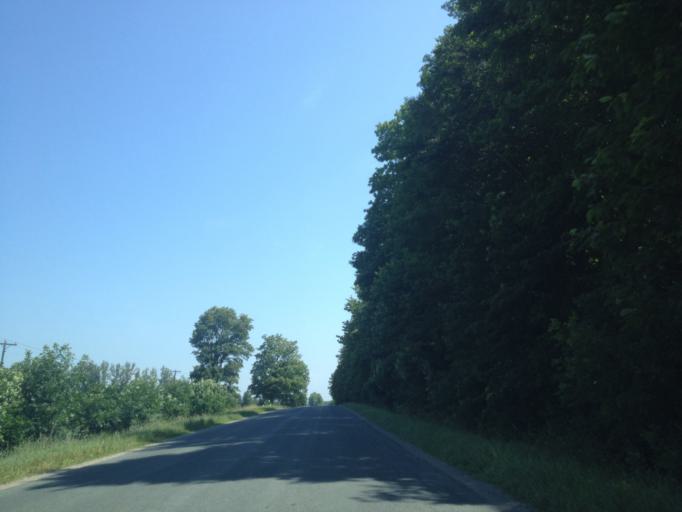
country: CA
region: Ontario
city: Stratford
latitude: 43.2620
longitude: -81.2020
